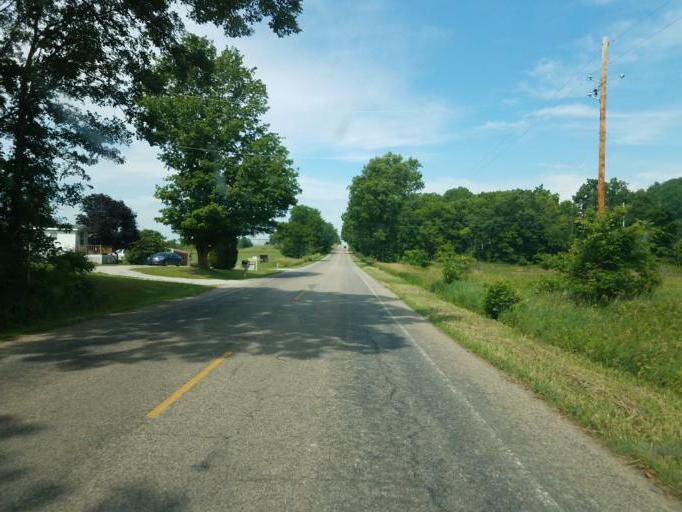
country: US
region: Michigan
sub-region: Barry County
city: Nashville
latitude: 42.6262
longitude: -84.9664
